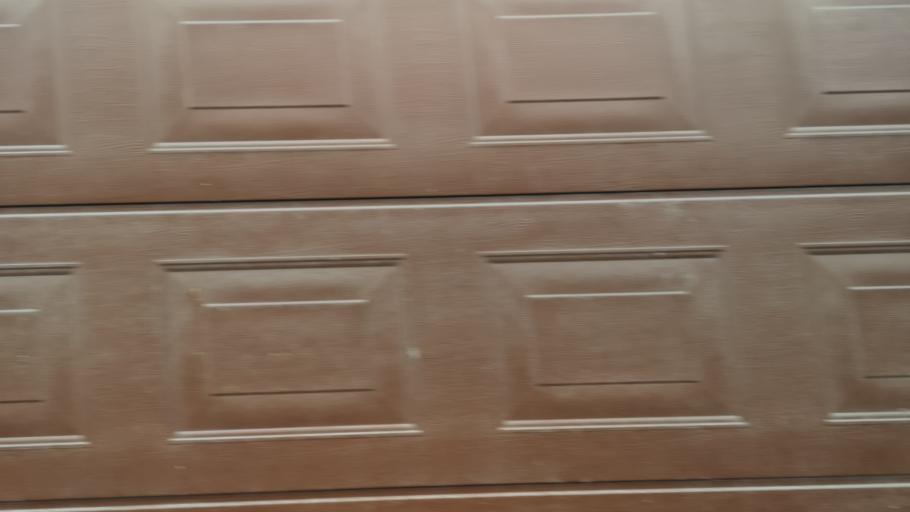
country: ES
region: Canary Islands
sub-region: Provincia de Santa Cruz de Tenerife
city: Hermigua
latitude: 28.1766
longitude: -17.1846
